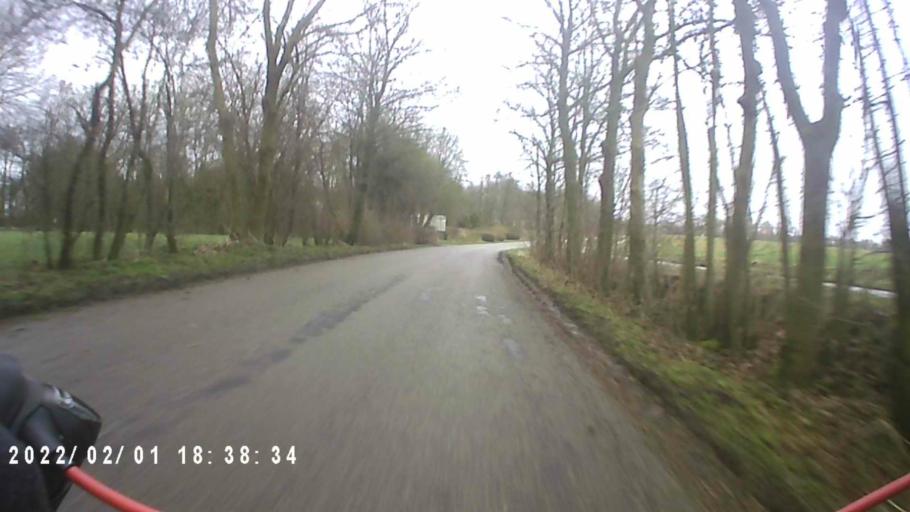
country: NL
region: Groningen
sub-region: Gemeente De Marne
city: Ulrum
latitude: 53.3610
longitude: 6.3646
